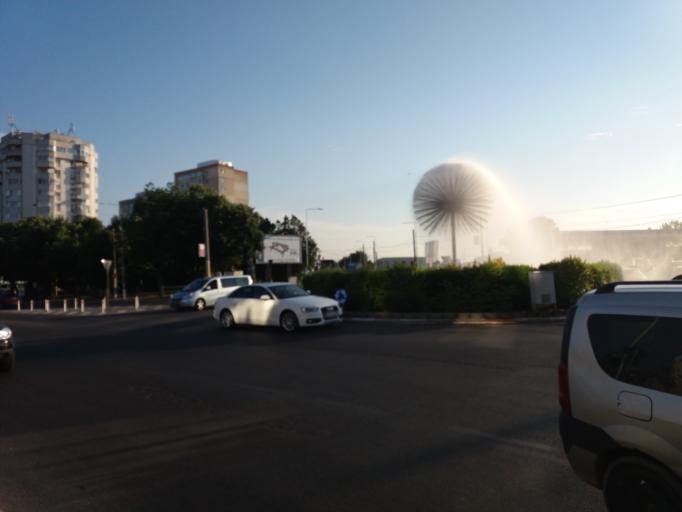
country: RO
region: Constanta
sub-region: Municipiul Constanta
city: Palazu Mare
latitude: 44.2170
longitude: 28.6284
